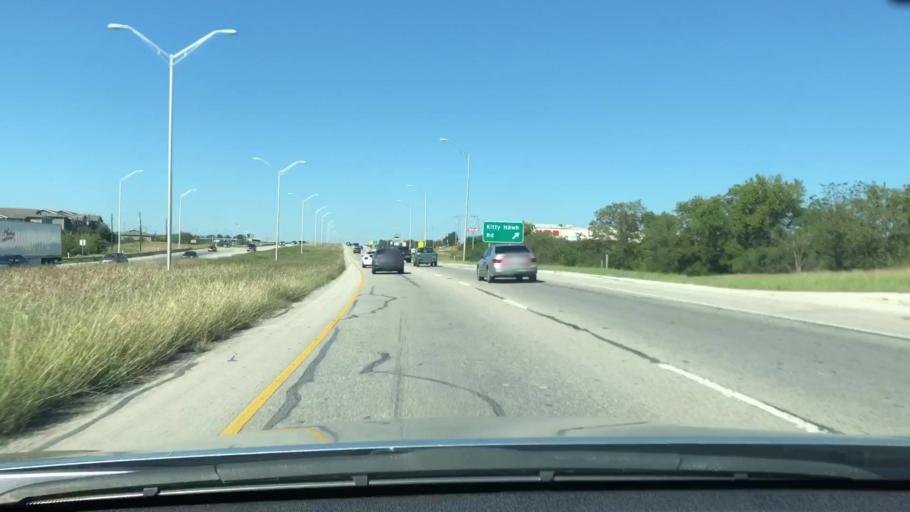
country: US
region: Texas
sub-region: Bexar County
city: Universal City
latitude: 29.5430
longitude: -98.3091
